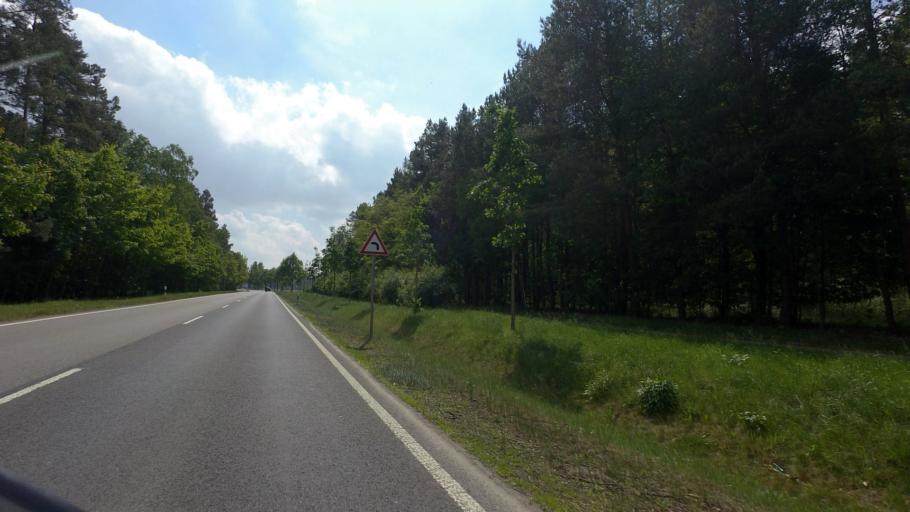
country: DE
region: Saxony
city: Weisskeissel
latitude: 51.4774
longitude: 14.7227
